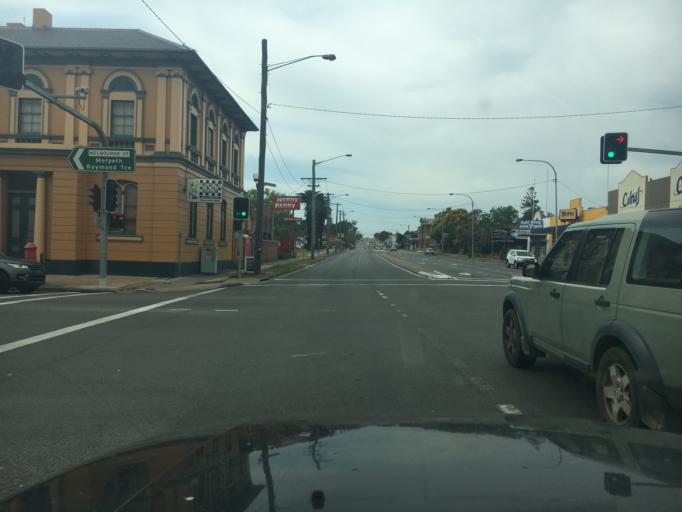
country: AU
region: New South Wales
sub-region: Maitland Municipality
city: East Maitland
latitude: -32.7465
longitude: 151.5815
